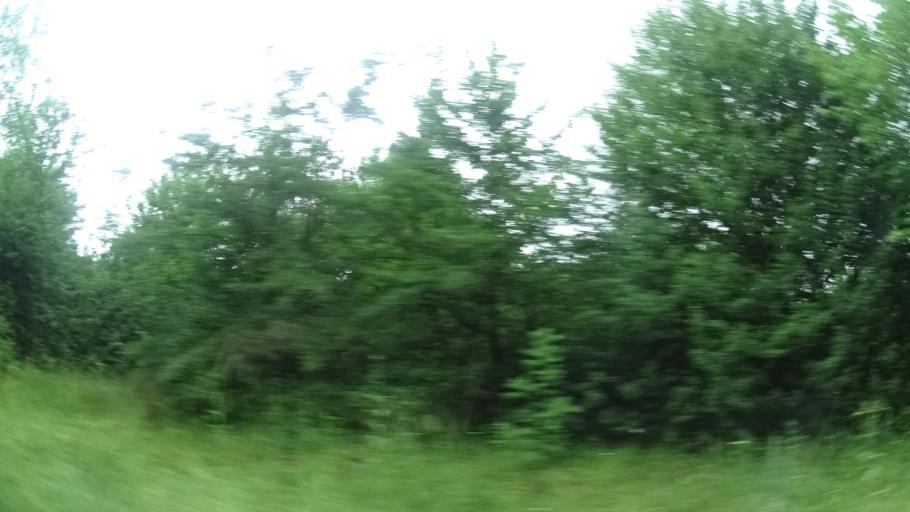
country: LU
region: Luxembourg
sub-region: Canton d'Esch-sur-Alzette
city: Bettembourg
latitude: 49.5051
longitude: 6.1322
